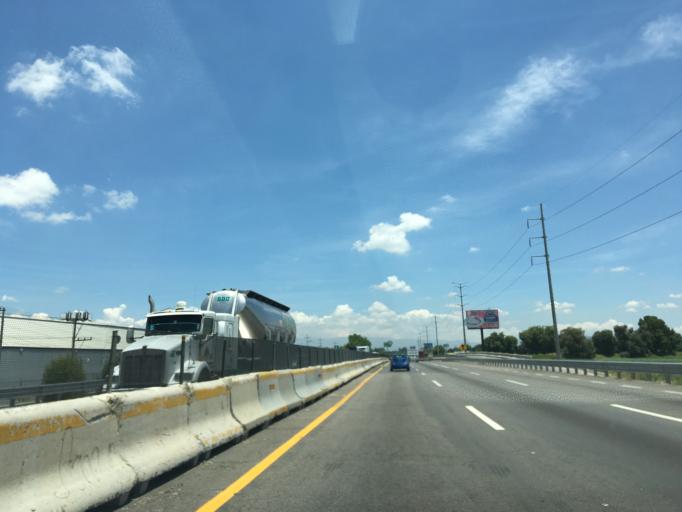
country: MX
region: Puebla
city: Santa Ana Xalmimilulco
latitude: 19.2275
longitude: -98.3717
